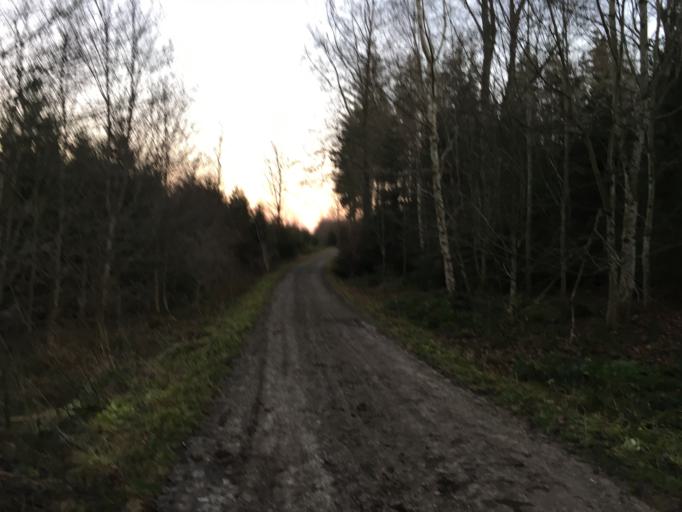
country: DE
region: Bavaria
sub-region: Swabia
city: Bohen
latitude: 47.8717
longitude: 10.2813
